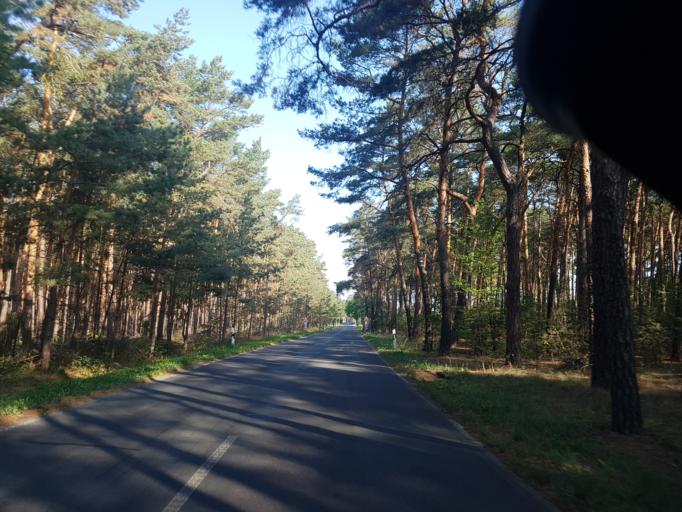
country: DE
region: Brandenburg
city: Niemegk
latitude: 52.1615
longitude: 12.6867
